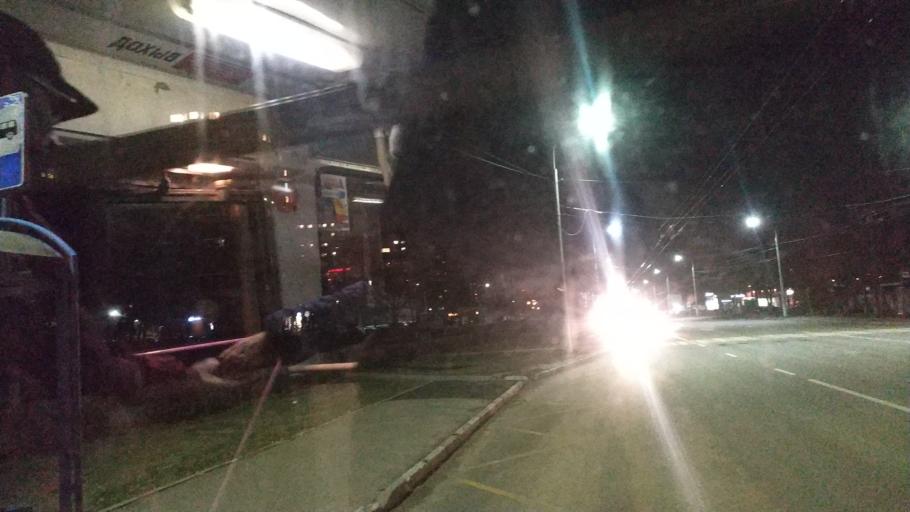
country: RU
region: Moskovskaya
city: Dubrovitsy
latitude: 55.4295
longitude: 37.5065
